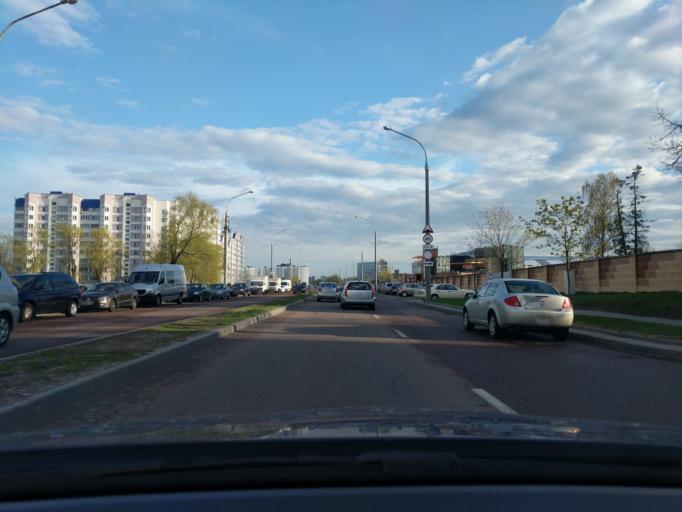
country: BY
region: Minsk
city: Novoye Medvezhino
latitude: 53.9064
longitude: 27.4731
